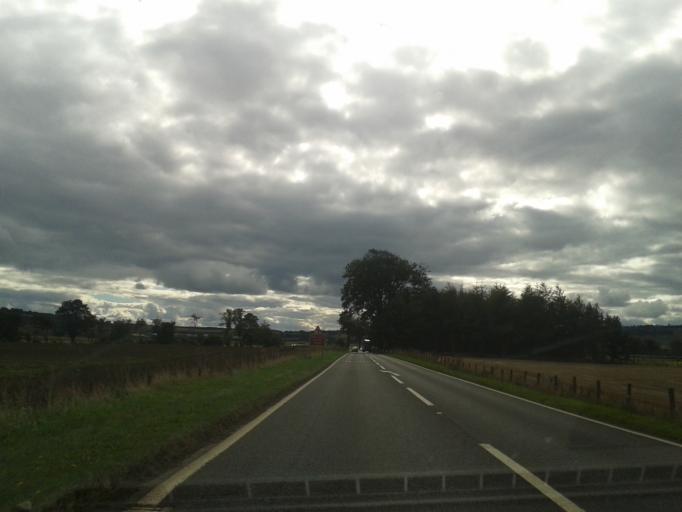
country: GB
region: Scotland
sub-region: Fife
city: Ladybank
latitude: 56.2675
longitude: -3.1411
